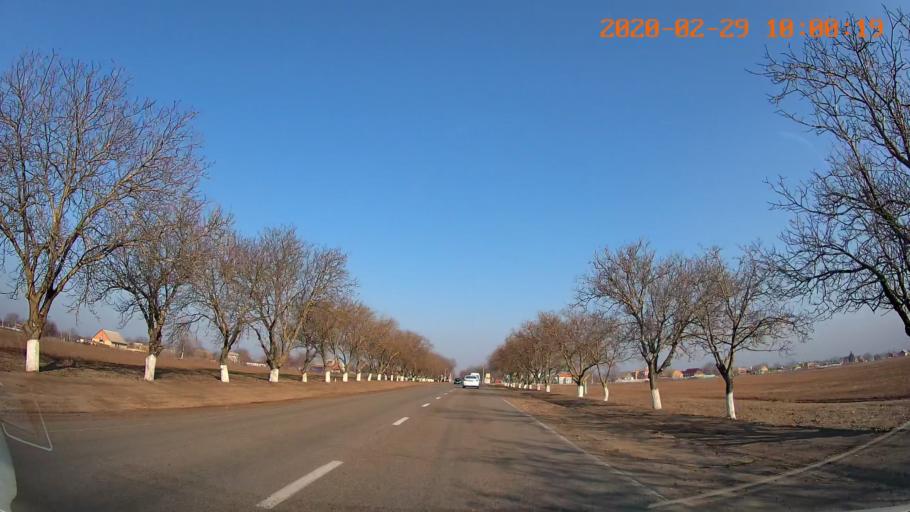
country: MD
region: Telenesti
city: Slobozia
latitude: 46.7670
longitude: 29.6865
